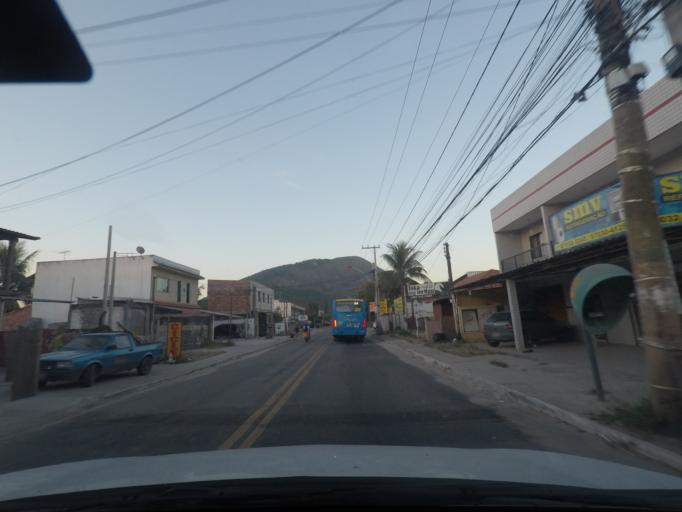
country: BR
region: Rio de Janeiro
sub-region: Marica
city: Marica
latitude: -22.9555
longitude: -42.9622
